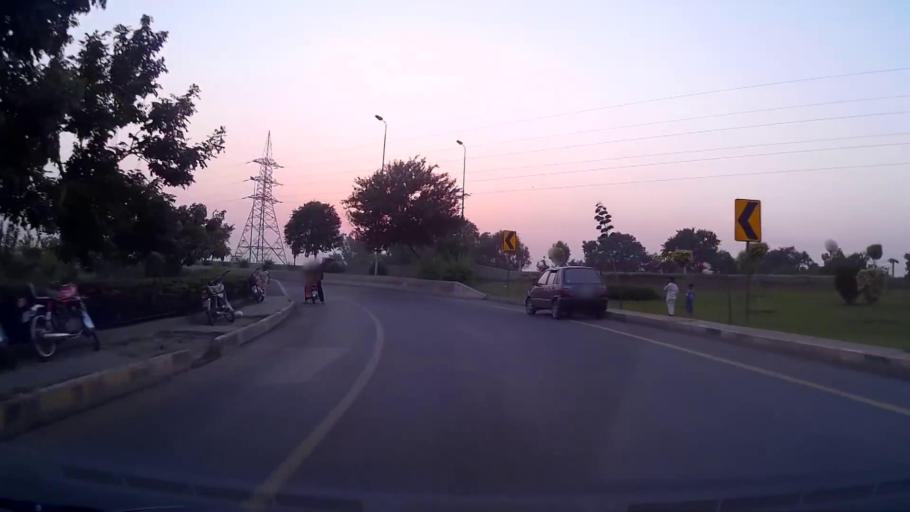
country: PK
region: Punjab
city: Lahore
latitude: 31.6051
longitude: 74.2972
